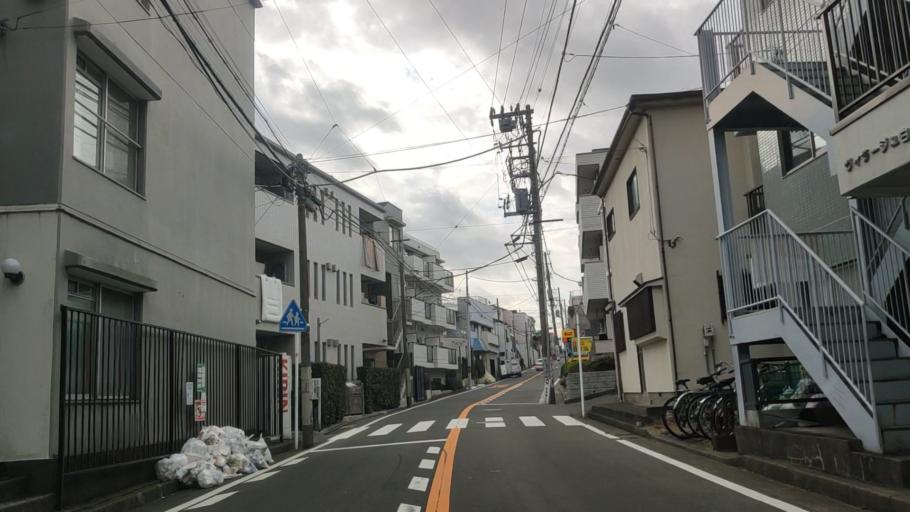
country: JP
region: Kanagawa
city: Yokohama
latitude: 35.4843
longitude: 139.6228
